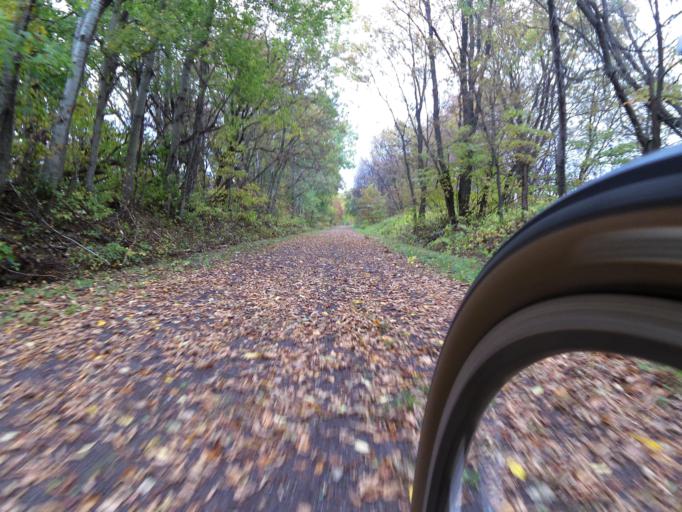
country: CA
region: Quebec
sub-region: Outaouais
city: Shawville
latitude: 45.6454
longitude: -76.5201
